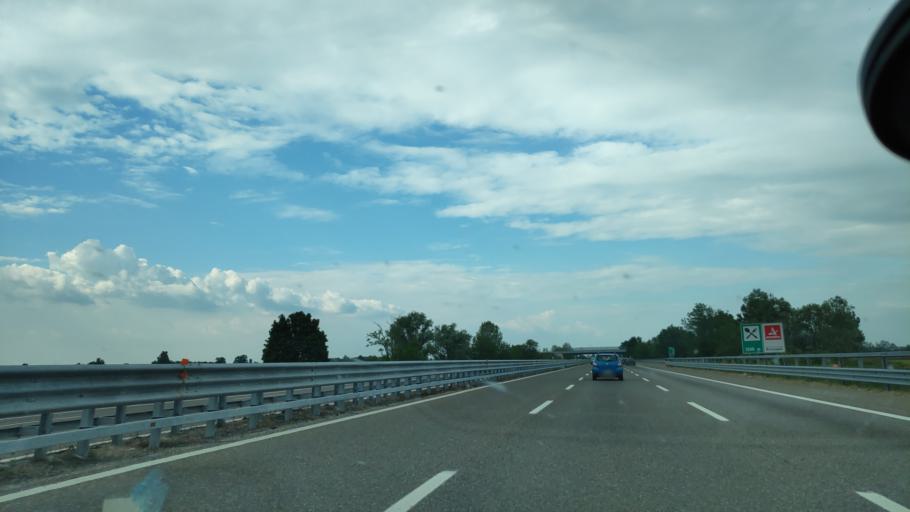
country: IT
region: Lombardy
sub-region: Provincia di Pavia
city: Pieve Albignola
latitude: 45.1333
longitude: 8.9824
